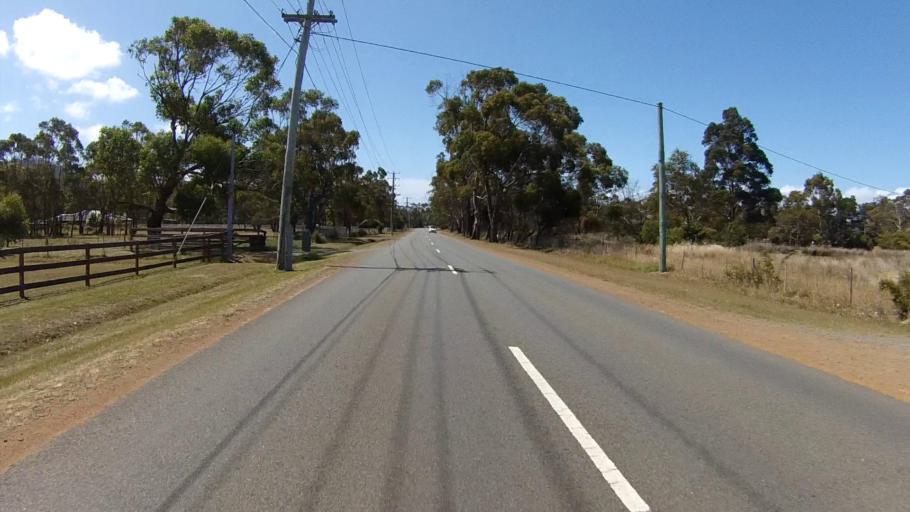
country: AU
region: Tasmania
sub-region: Clarence
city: Sandford
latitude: -42.9490
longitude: 147.4815
